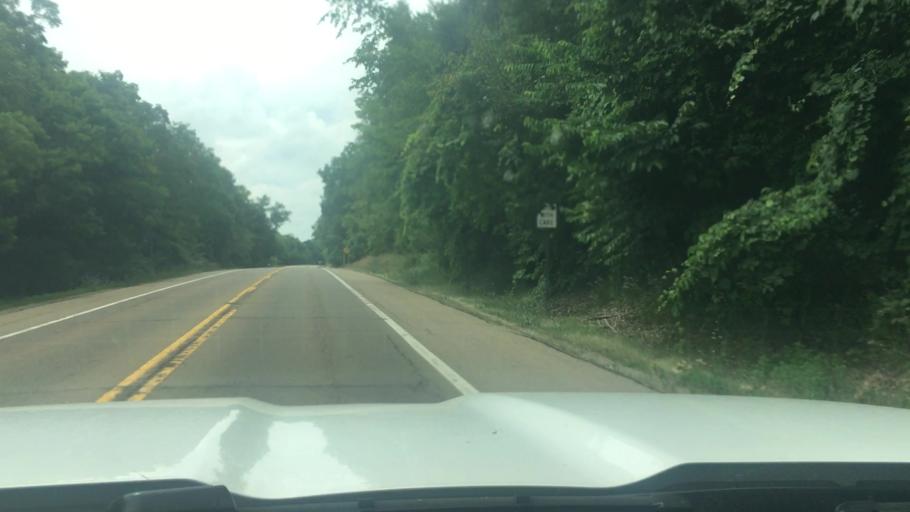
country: US
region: Michigan
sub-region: Kent County
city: Lowell
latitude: 42.9255
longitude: -85.4052
